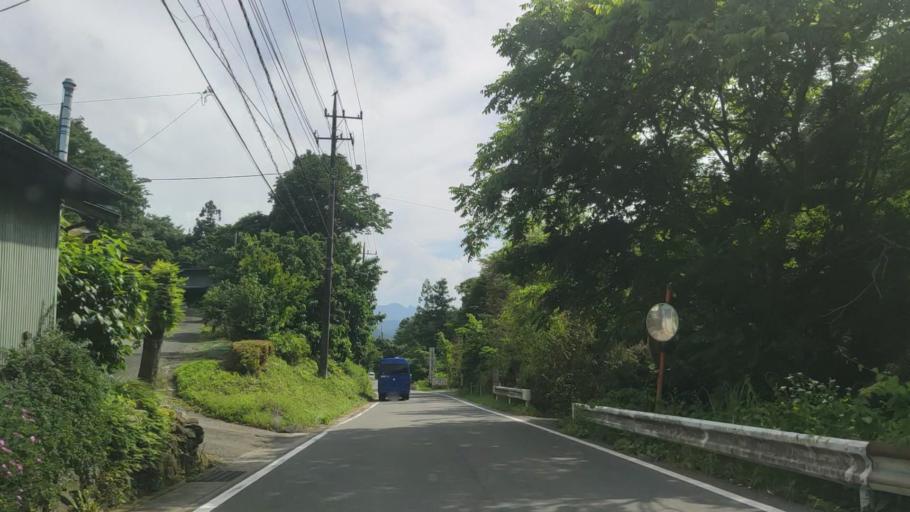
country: JP
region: Gunma
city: Tomioka
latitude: 36.1943
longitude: 138.7539
